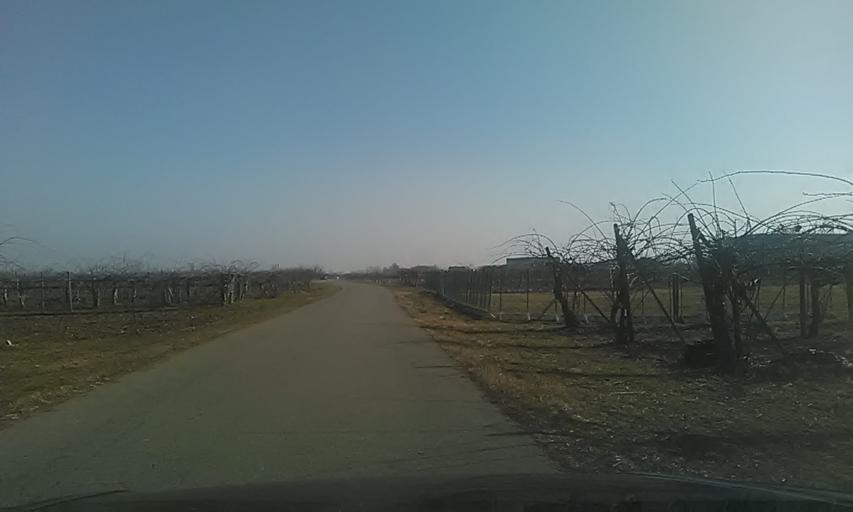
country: IT
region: Piedmont
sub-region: Provincia di Vercelli
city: Borgo d'Ale
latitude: 45.3462
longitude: 8.0633
